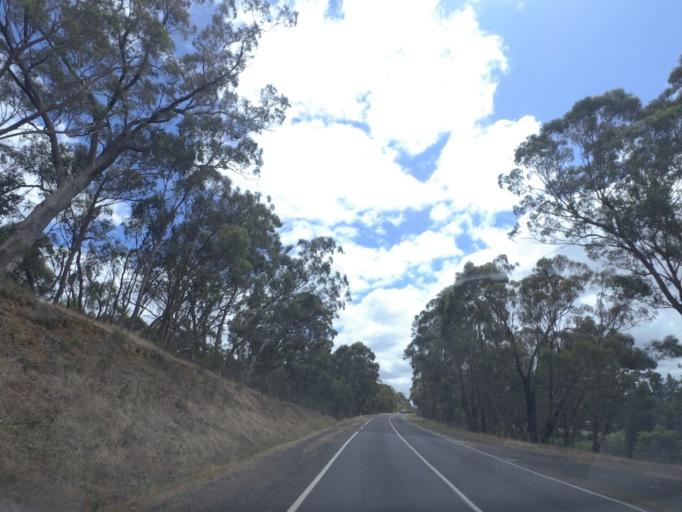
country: AU
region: Victoria
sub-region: Whittlesea
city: Whittlesea
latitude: -37.2360
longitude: 145.0458
